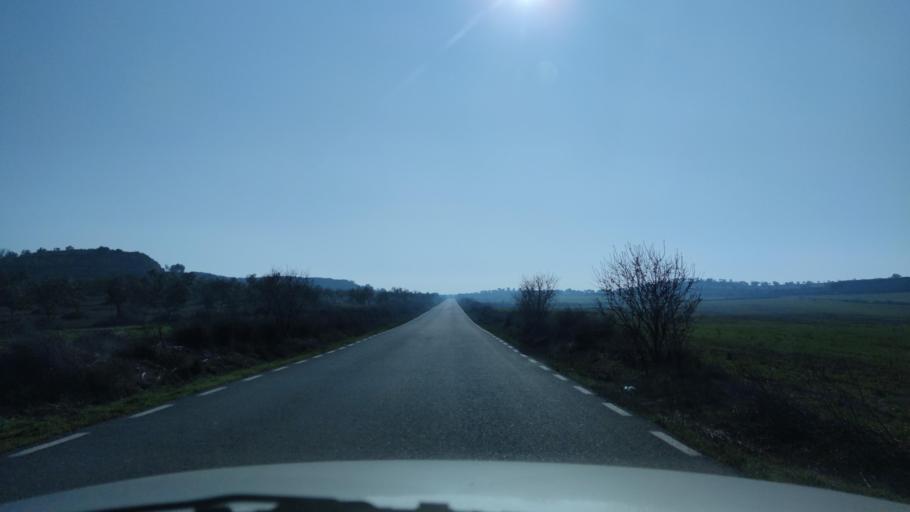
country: ES
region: Catalonia
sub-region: Provincia de Lleida
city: Alcano
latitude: 41.4744
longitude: 0.5613
